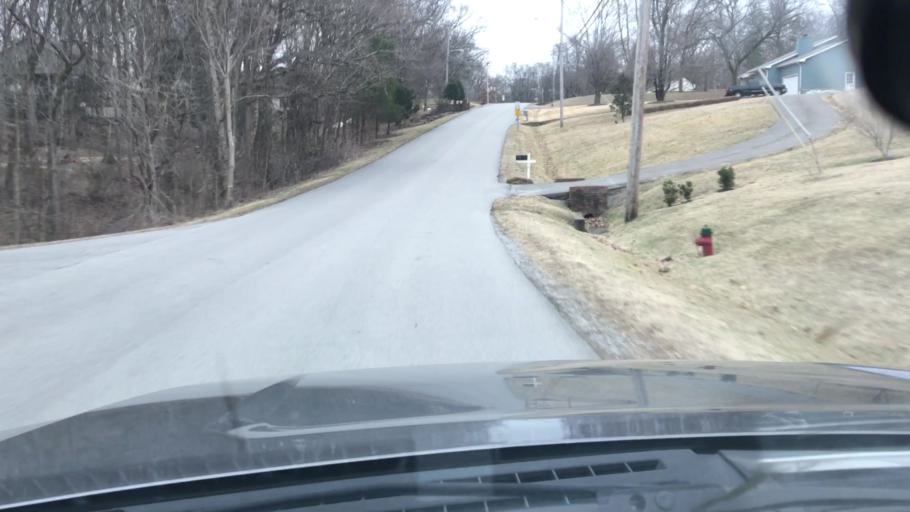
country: US
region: Tennessee
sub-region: Williamson County
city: Brentwood Estates
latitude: 36.0068
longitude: -86.7196
